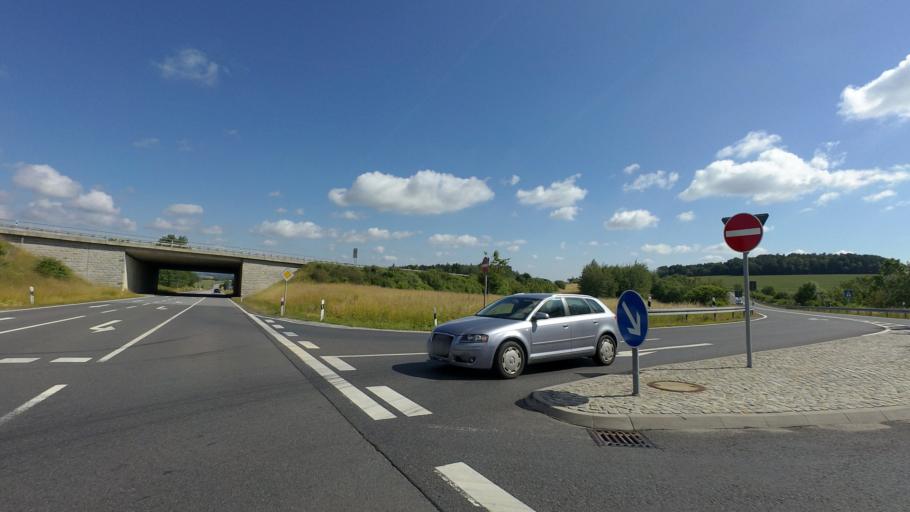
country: DE
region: Saxony
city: Rammenau
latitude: 51.1747
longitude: 14.1403
